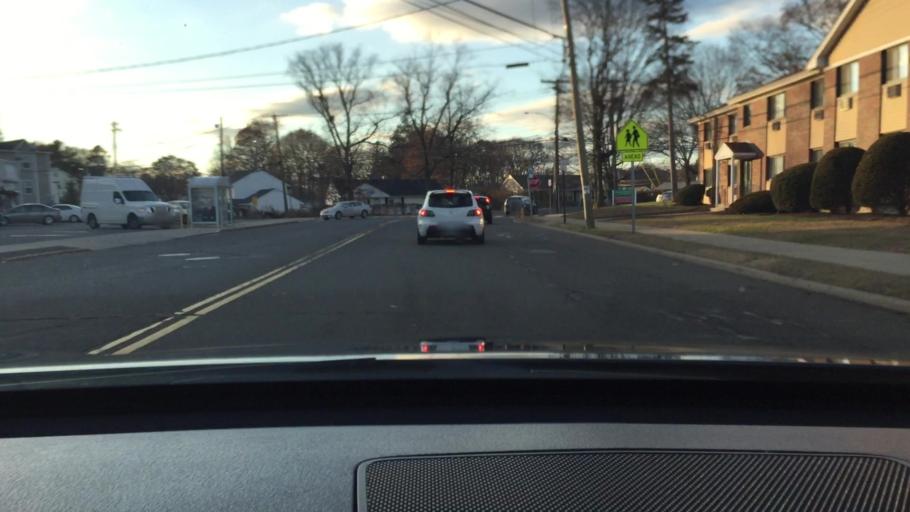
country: US
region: Connecticut
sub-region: Fairfield County
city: Trumbull
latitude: 41.2224
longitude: -73.2301
